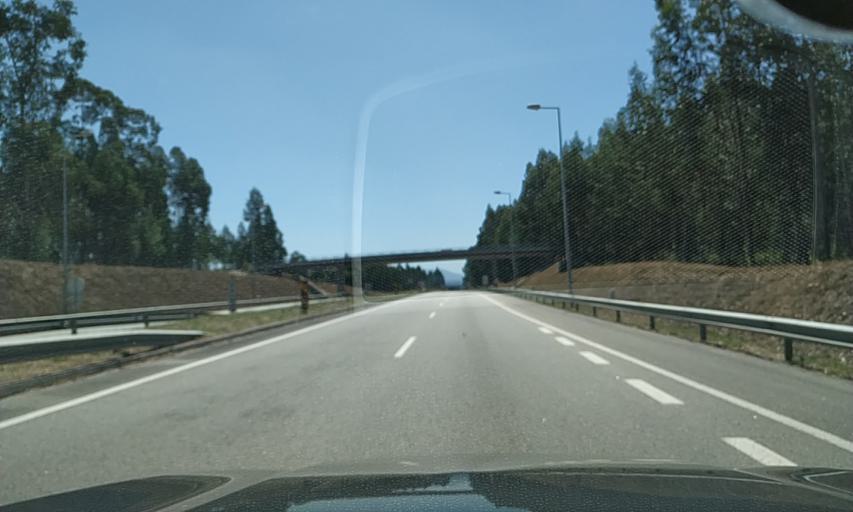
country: PT
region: Aveiro
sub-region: Agueda
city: Agueda
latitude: 40.5512
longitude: -8.4723
